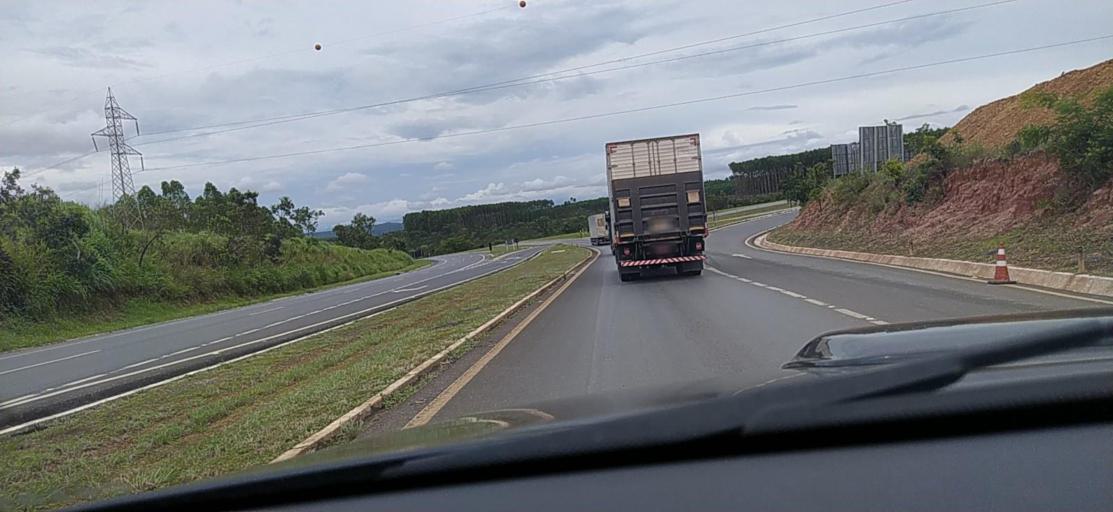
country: BR
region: Minas Gerais
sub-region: Curvelo
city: Curvelo
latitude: -18.7061
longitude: -44.4409
